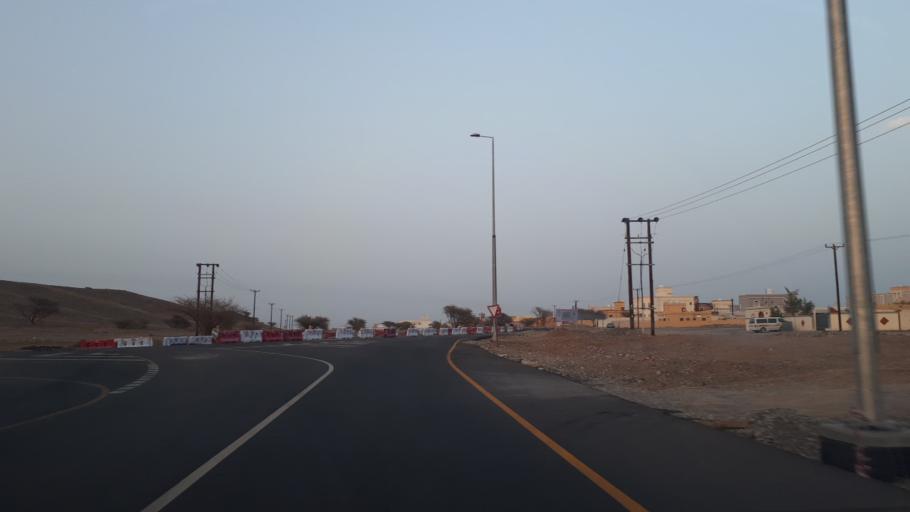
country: OM
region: Al Batinah
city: Rustaq
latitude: 23.5419
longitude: 57.5266
